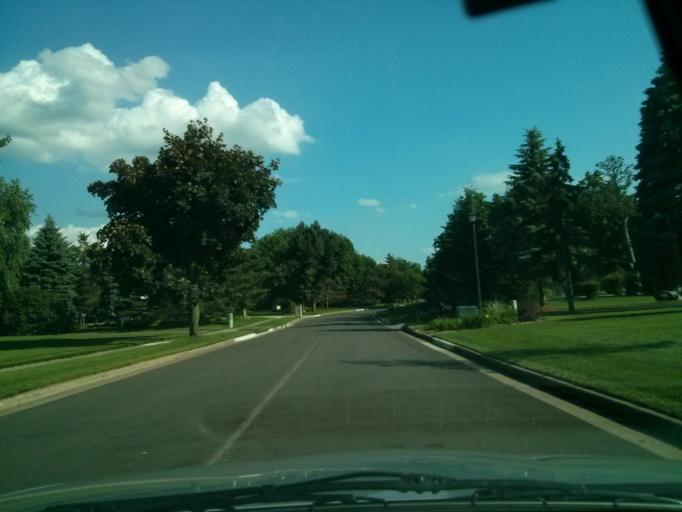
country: US
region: Wisconsin
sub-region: Saint Croix County
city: Hudson
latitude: 44.9594
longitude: -92.7462
